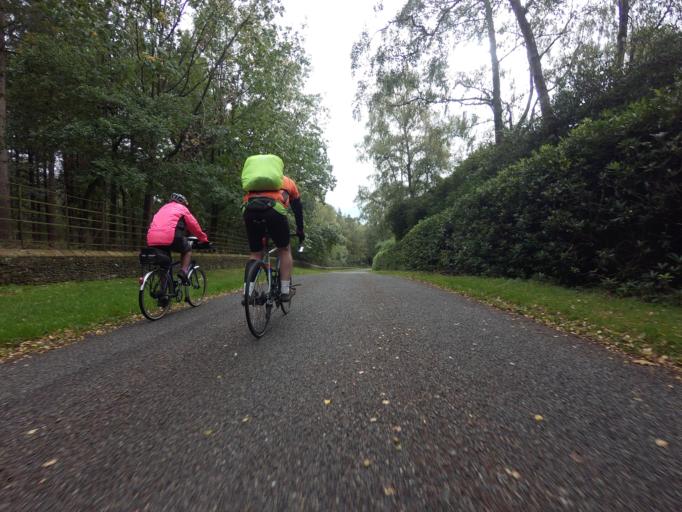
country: GB
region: England
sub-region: Norfolk
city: Dersingham
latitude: 52.8229
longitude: 0.4963
